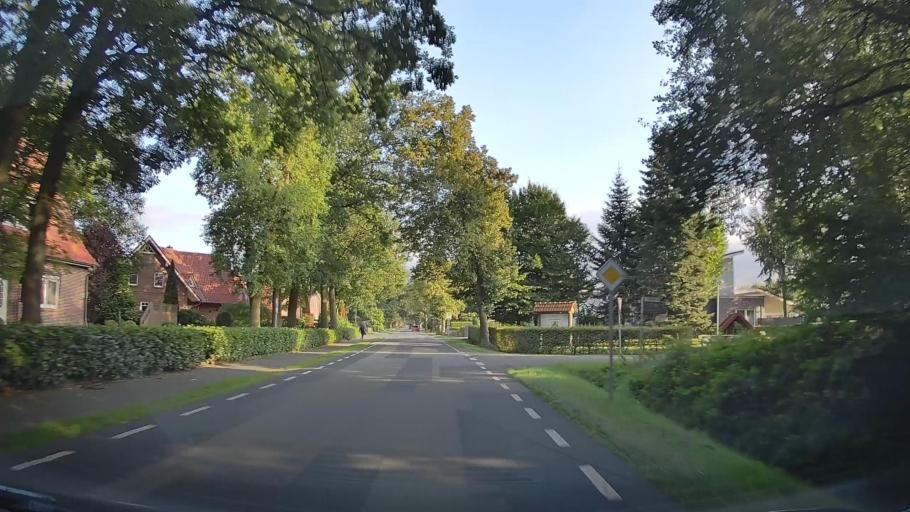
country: DE
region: Lower Saxony
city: Hilkenbrook
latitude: 53.0153
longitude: 7.7584
